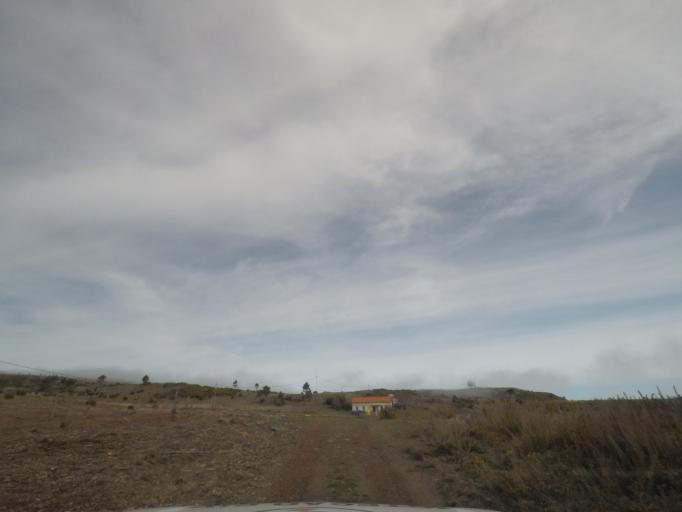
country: PT
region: Madeira
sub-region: Funchal
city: Nossa Senhora do Monte
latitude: 32.7128
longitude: -16.9080
